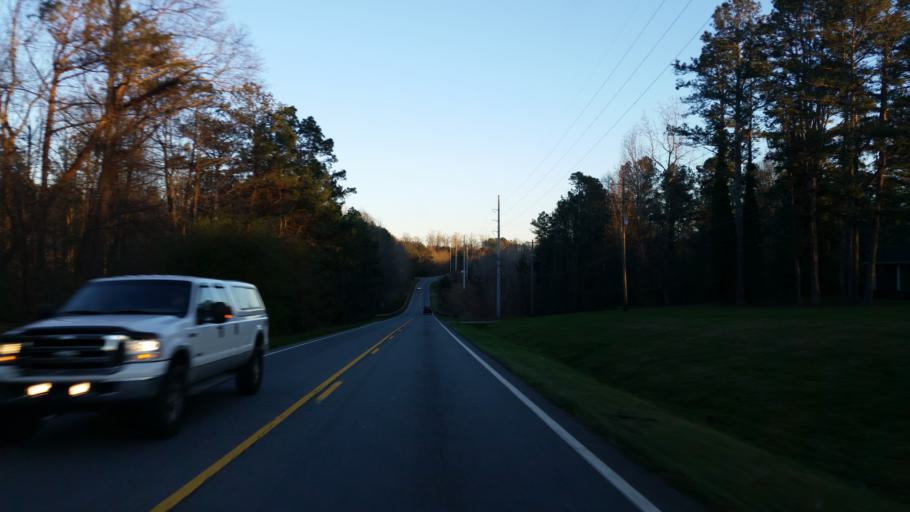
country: US
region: Georgia
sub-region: Dawson County
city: Dawsonville
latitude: 34.3503
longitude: -84.0292
